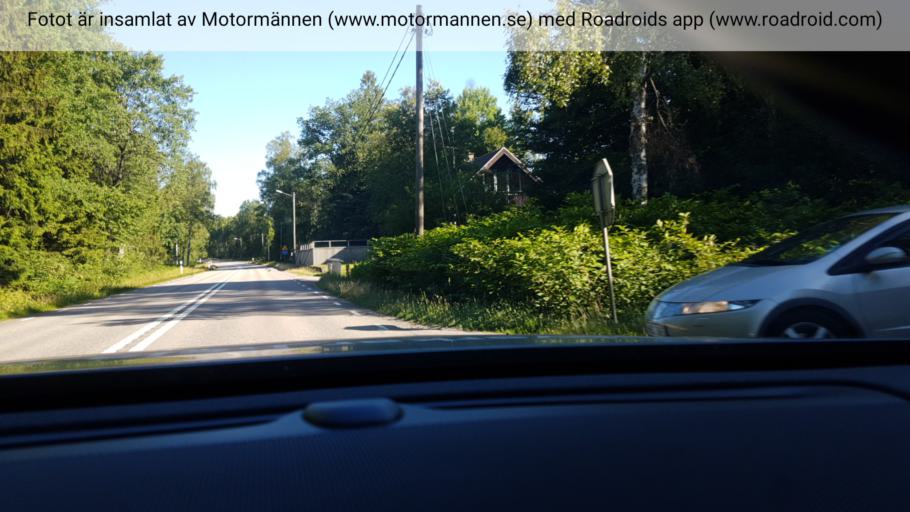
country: SE
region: Kronoberg
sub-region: Markaryds Kommun
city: Markaryd
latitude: 56.4049
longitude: 13.6454
